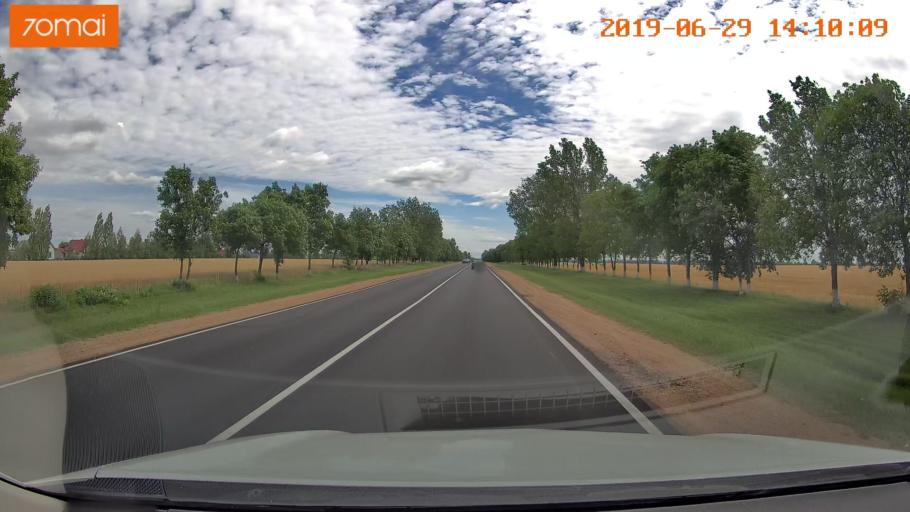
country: BY
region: Minsk
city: Salihorsk
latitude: 52.8328
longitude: 27.4916
